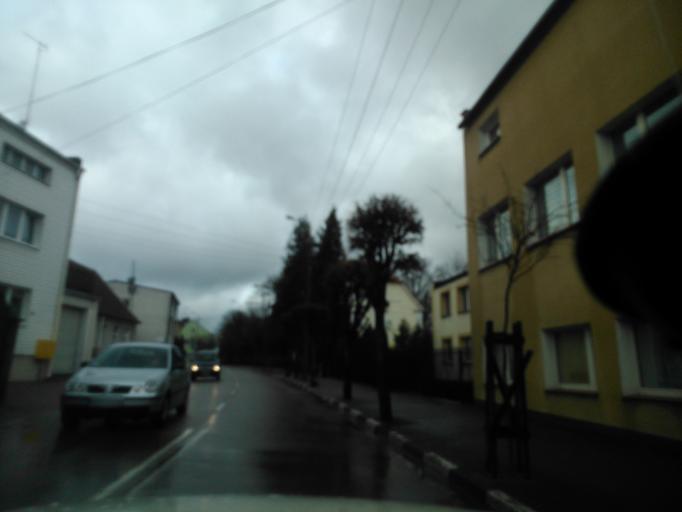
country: PL
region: Warmian-Masurian Voivodeship
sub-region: Powiat dzialdowski
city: Lidzbark
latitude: 53.2652
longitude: 19.8210
